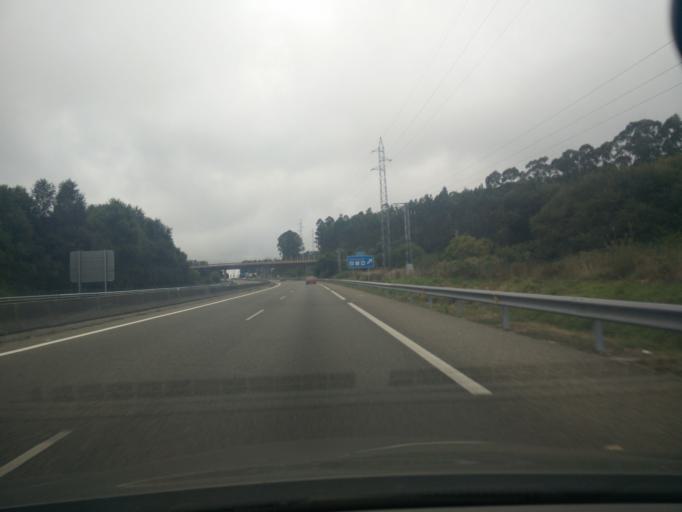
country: ES
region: Galicia
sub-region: Provincia da Coruna
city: Arteixo
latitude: 43.2711
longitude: -8.5338
